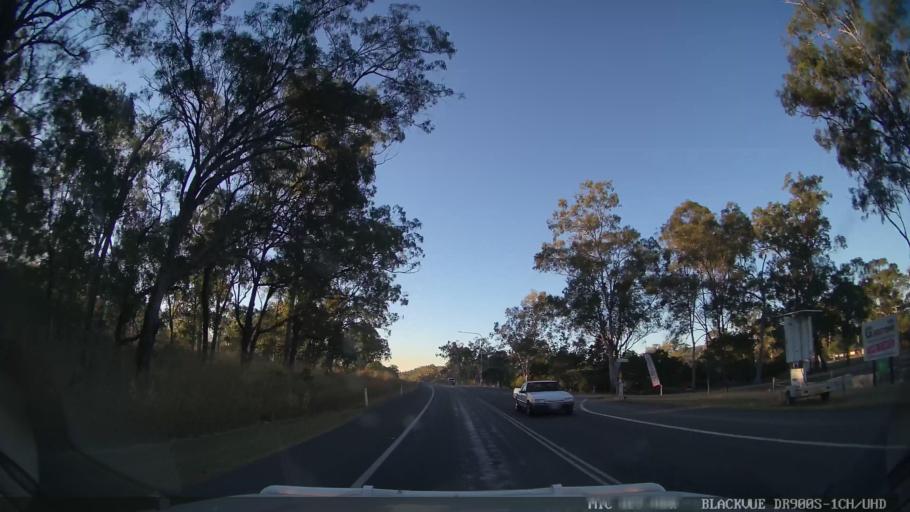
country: AU
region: Queensland
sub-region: Gladstone
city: Toolooa
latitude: -23.9561
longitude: 151.2201
